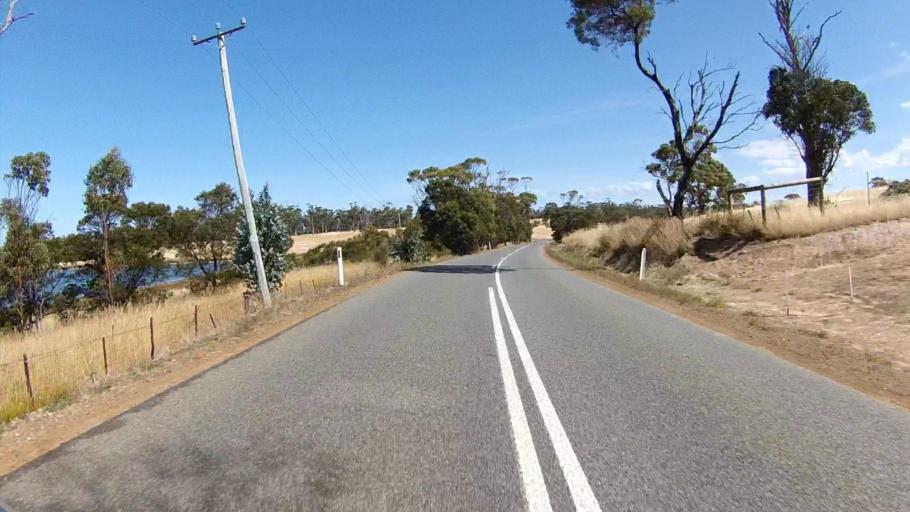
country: AU
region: Tasmania
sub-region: Sorell
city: Sorell
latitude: -42.2791
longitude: 148.0021
